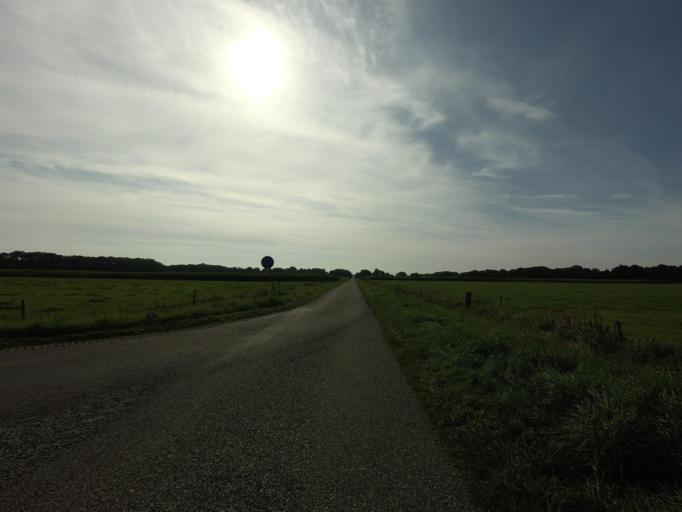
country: NL
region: Drenthe
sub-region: Gemeente Aa en Hunze
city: Anloo
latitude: 52.9442
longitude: 6.6741
